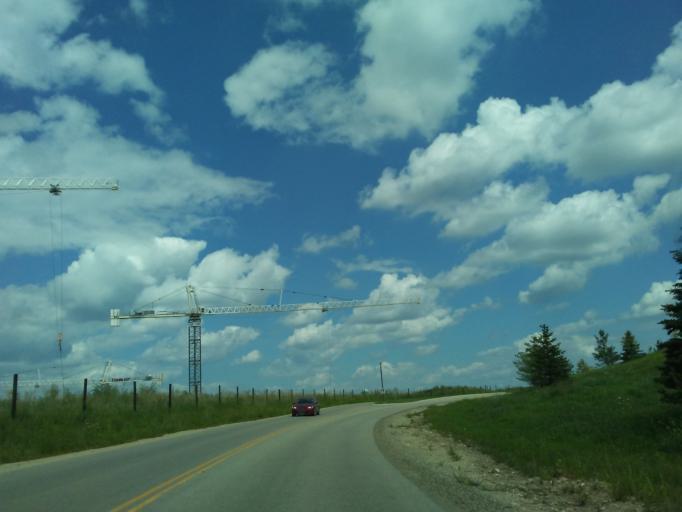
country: US
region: Wisconsin
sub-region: Dane County
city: Verona
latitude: 42.9968
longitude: -89.5626
